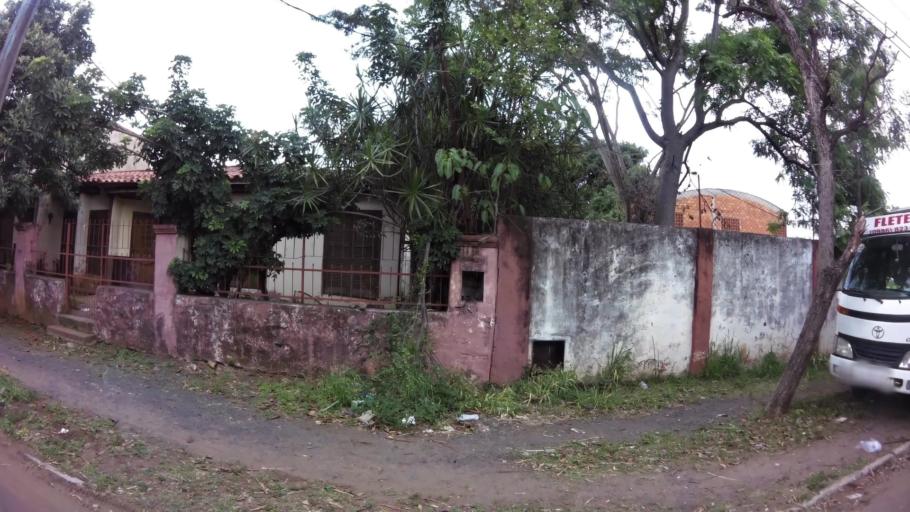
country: PY
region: Central
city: Fernando de la Mora
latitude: -25.3335
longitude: -57.5599
